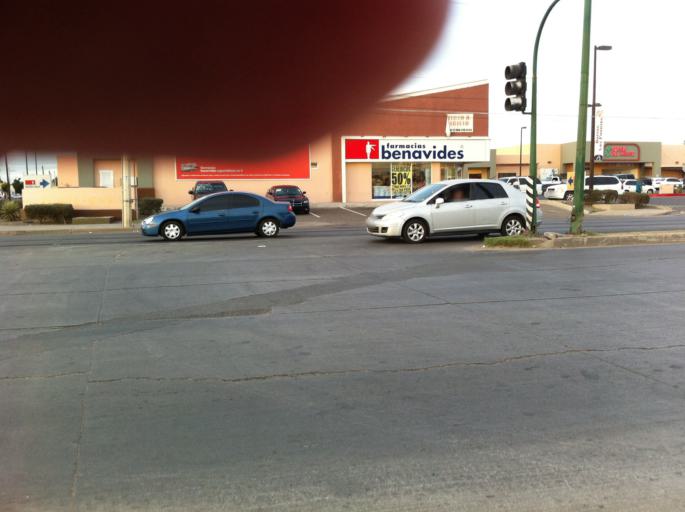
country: MX
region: Sonora
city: Hermosillo
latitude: 29.1165
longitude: -110.9990
